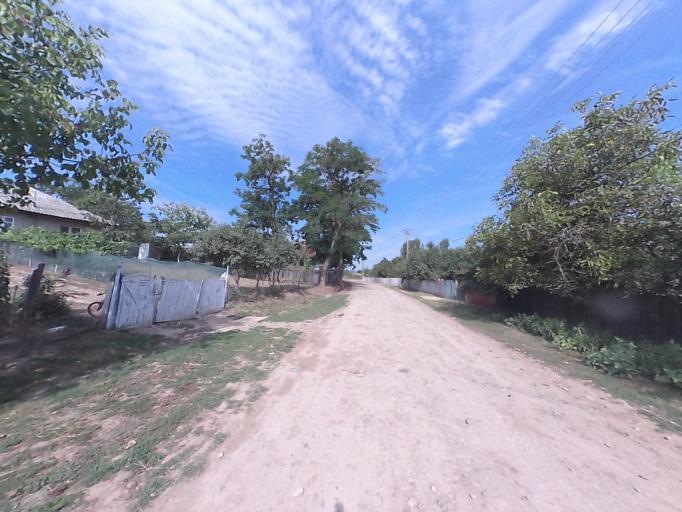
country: RO
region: Vaslui
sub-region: Comuna Osesti
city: Buda
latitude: 46.7619
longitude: 27.4205
